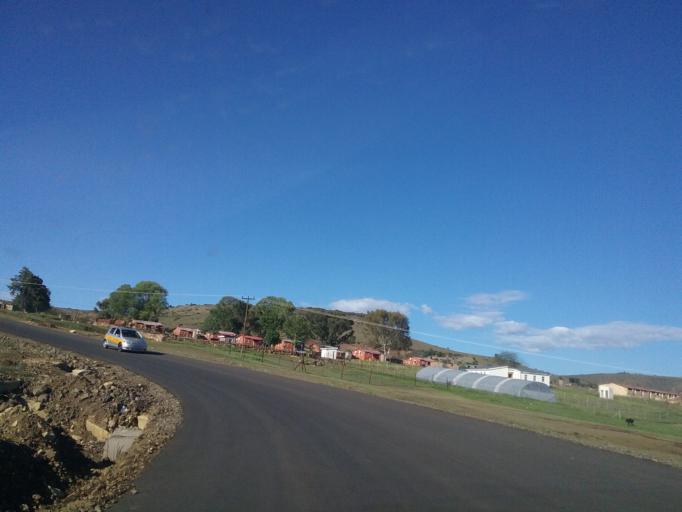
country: LS
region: Quthing
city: Quthing
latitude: -30.4054
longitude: 27.7014
